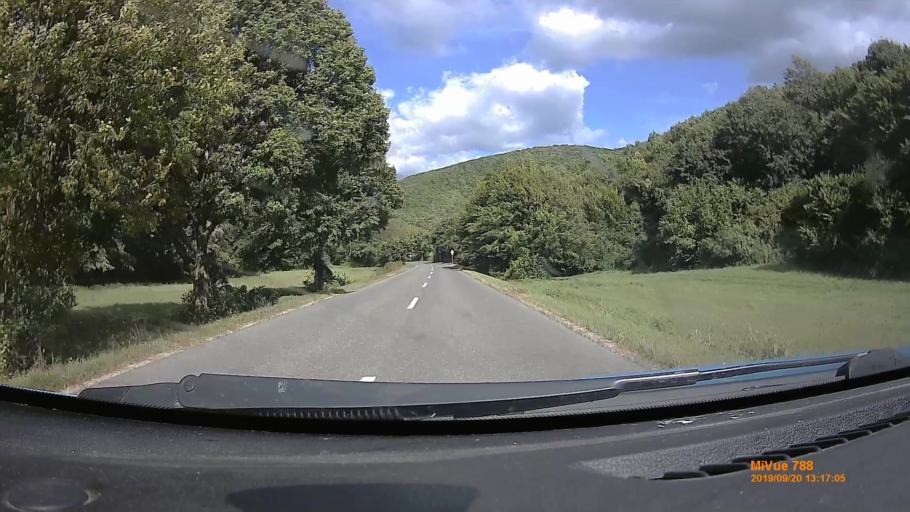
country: HU
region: Heves
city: Felsotarkany
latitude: 47.9896
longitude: 20.4573
